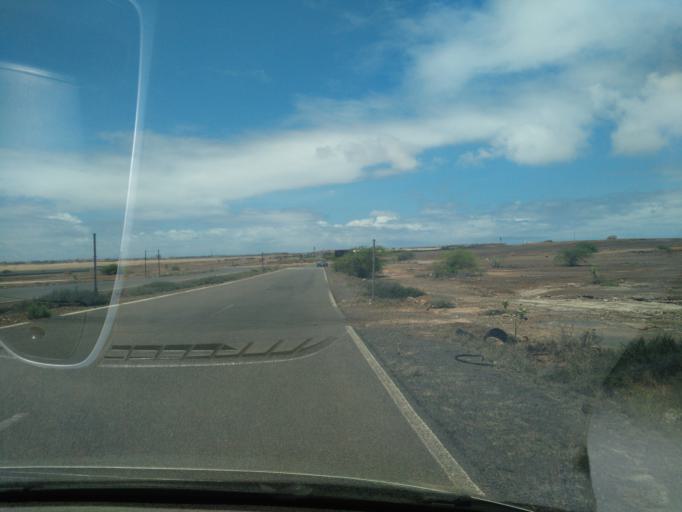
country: CV
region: Sal
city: Santa Maria
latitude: 16.6310
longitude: -22.9170
